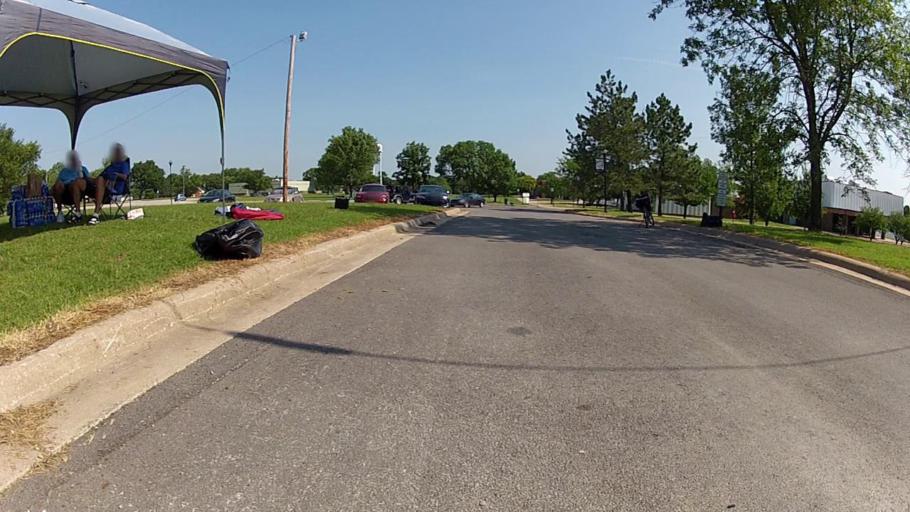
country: US
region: Kansas
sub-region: Montgomery County
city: Independence
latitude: 37.1930
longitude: -95.7216
